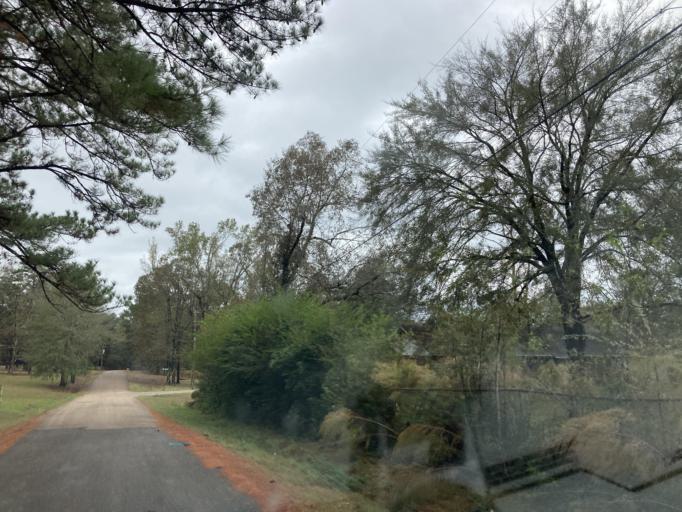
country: US
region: Mississippi
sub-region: Lamar County
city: West Hattiesburg
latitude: 31.2913
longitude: -89.4743
